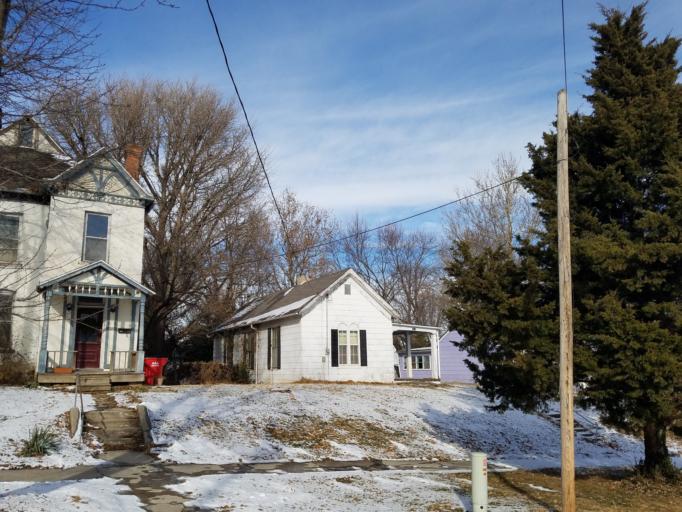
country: US
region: Missouri
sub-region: Lafayette County
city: Lexington
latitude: 39.1878
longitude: -93.8849
